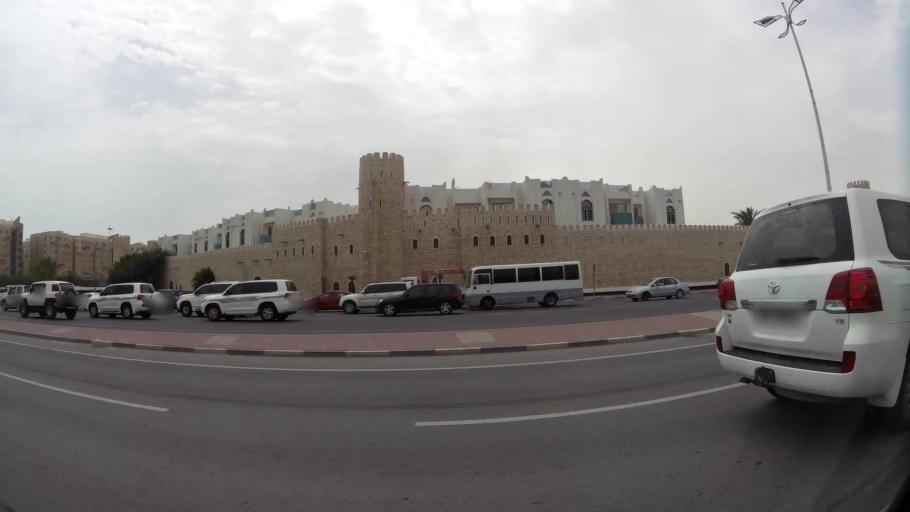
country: QA
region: Baladiyat ad Dawhah
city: Doha
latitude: 25.2991
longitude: 51.5008
